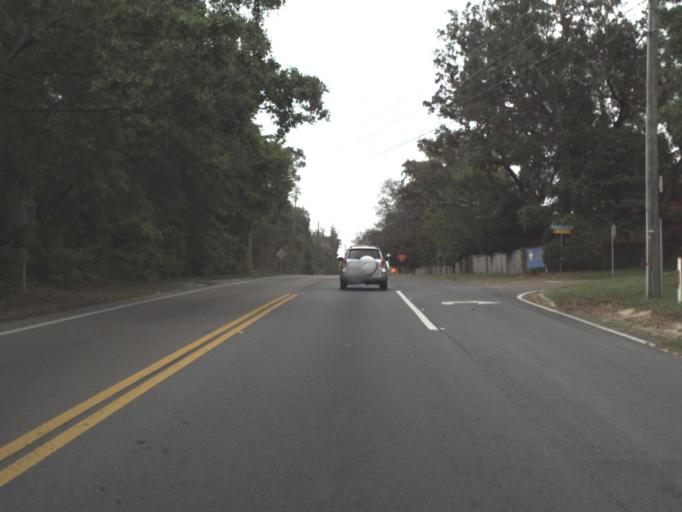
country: US
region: Florida
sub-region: Escambia County
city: Ferry Pass
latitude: 30.5190
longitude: -87.1709
